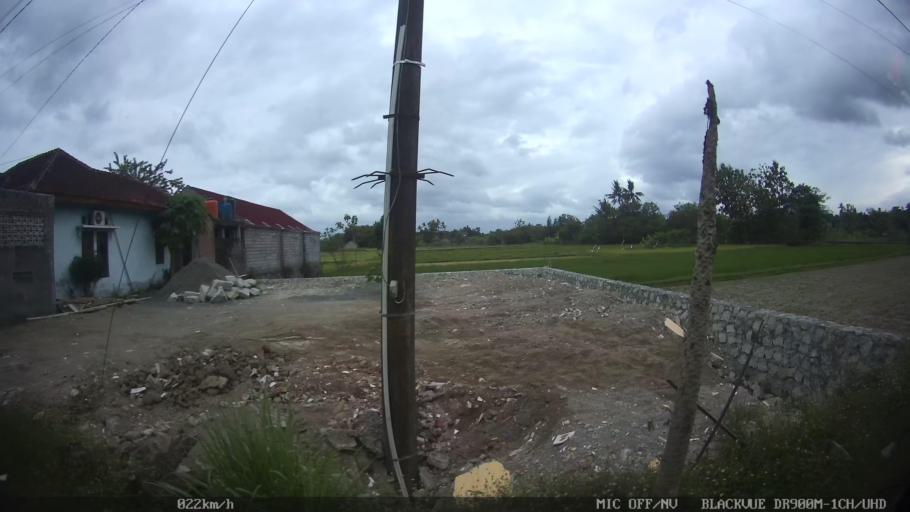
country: ID
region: Daerah Istimewa Yogyakarta
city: Sewon
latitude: -7.8497
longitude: 110.4154
